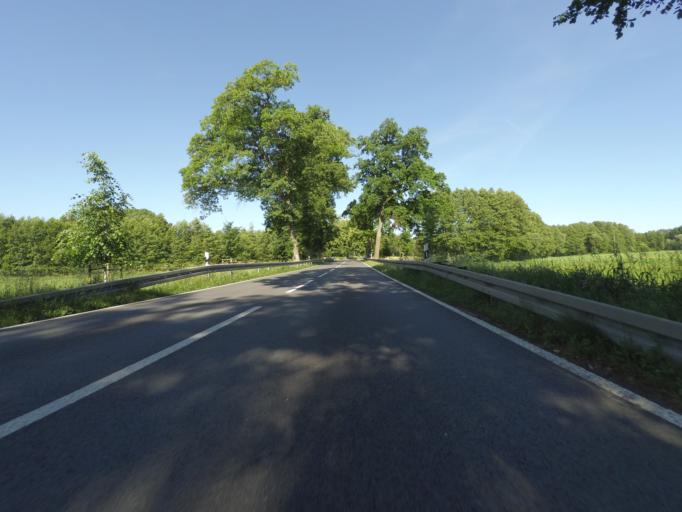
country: DE
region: Brandenburg
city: Triglitz
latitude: 53.2112
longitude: 12.0960
